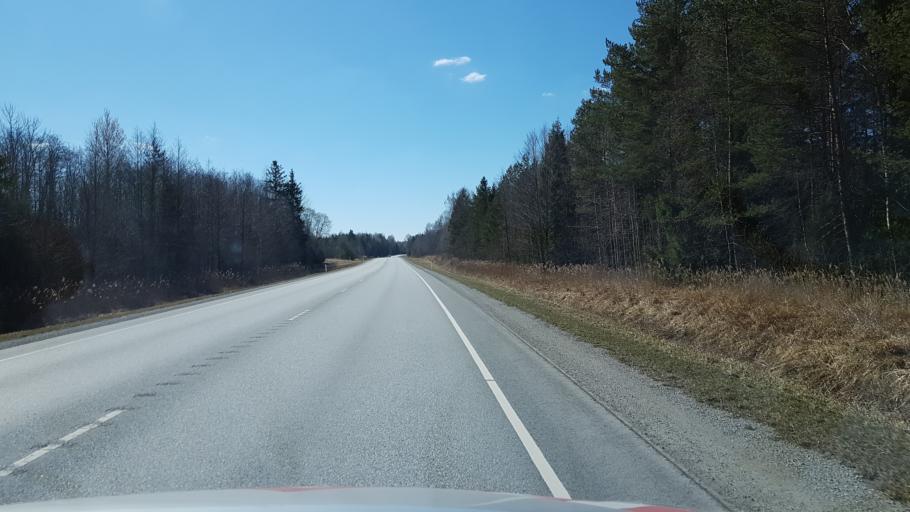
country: EE
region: Harju
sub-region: Nissi vald
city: Riisipere
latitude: 59.1579
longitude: 24.3419
